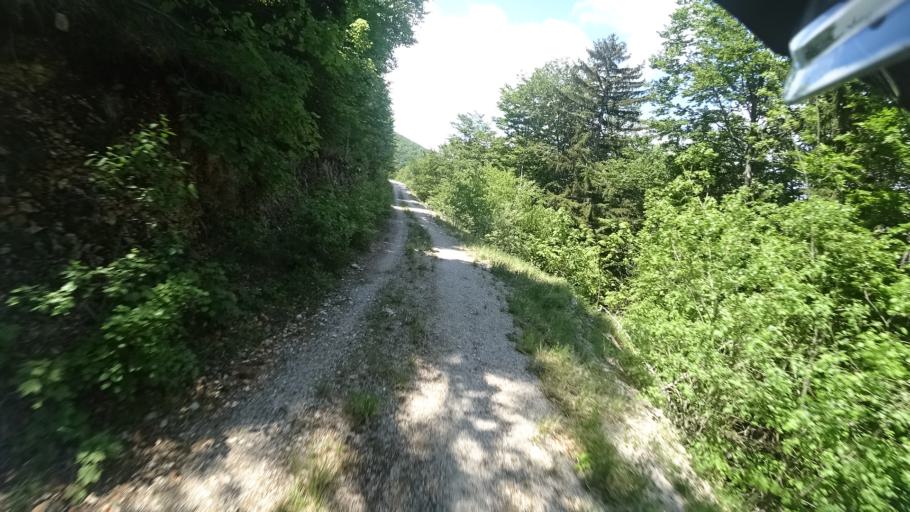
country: BA
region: Federation of Bosnia and Herzegovina
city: Orasac
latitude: 44.5689
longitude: 15.8542
